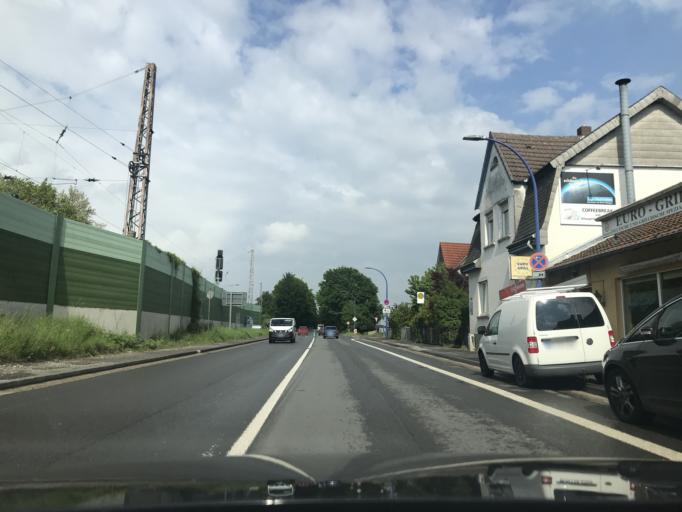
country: DE
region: North Rhine-Westphalia
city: Schwerte
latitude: 51.4188
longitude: 7.5294
